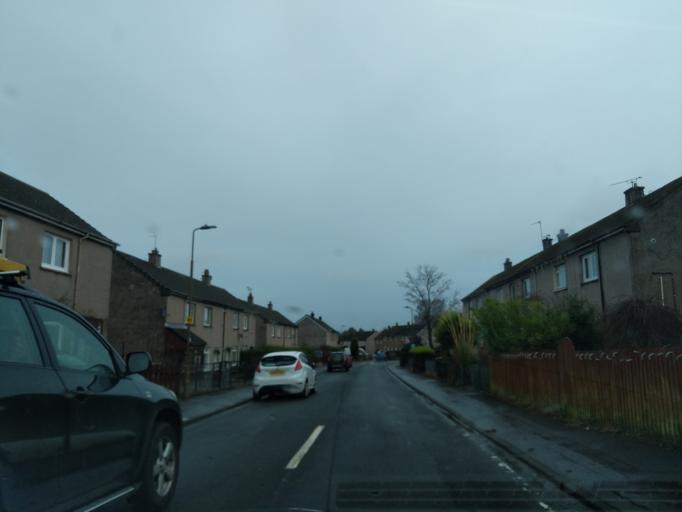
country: GB
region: Scotland
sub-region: Edinburgh
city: Balerno
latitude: 55.8804
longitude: -3.3451
